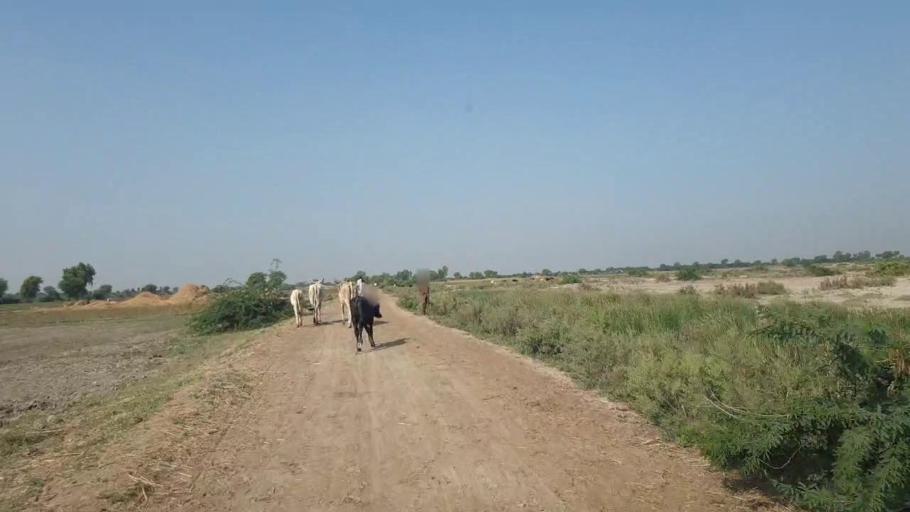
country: PK
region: Sindh
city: Badin
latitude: 24.5236
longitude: 68.7531
